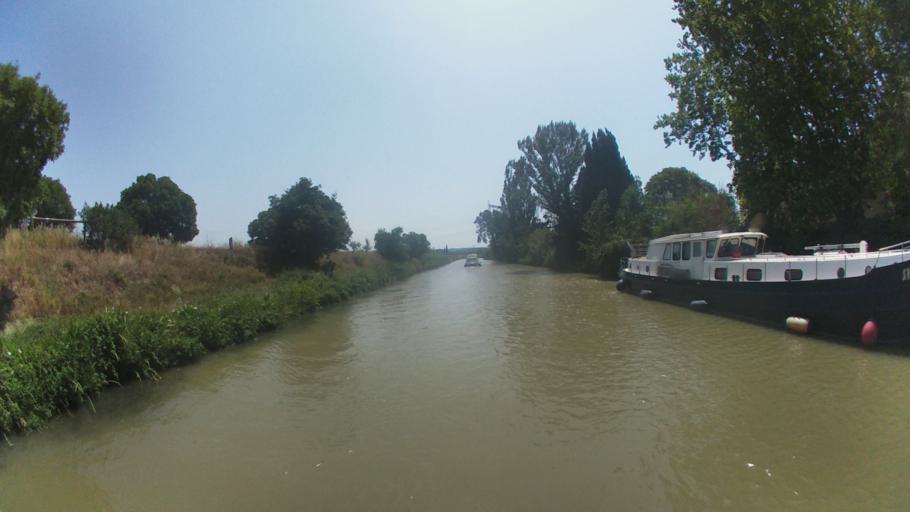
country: FR
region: Languedoc-Roussillon
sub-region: Departement de l'Aude
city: Azille
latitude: 43.2473
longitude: 2.6598
